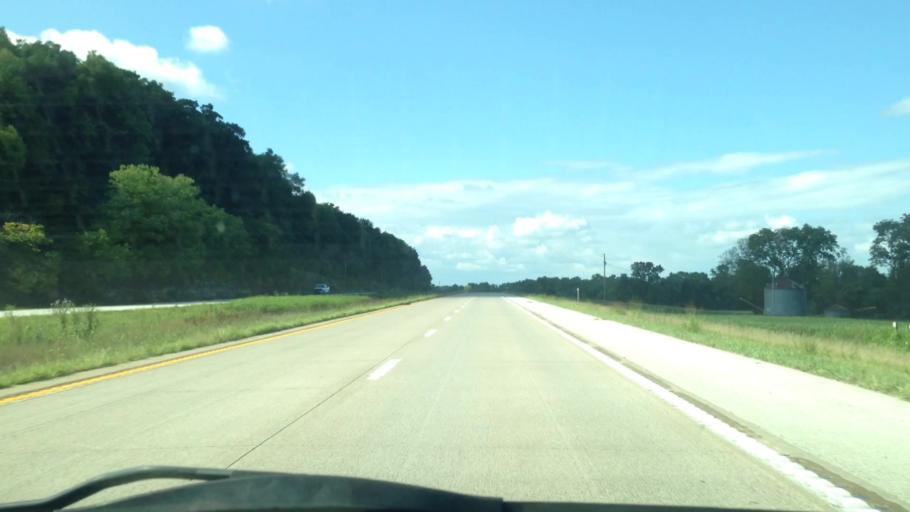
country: US
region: Missouri
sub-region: Lewis County
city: Canton
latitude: 40.2292
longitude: -91.5305
